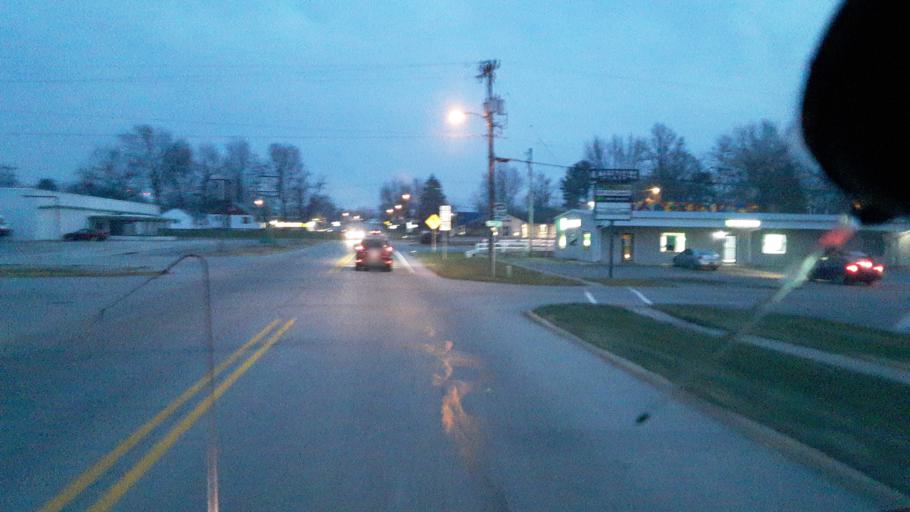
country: US
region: Indiana
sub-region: LaGrange County
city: Lagrange
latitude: 41.6384
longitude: -85.4178
